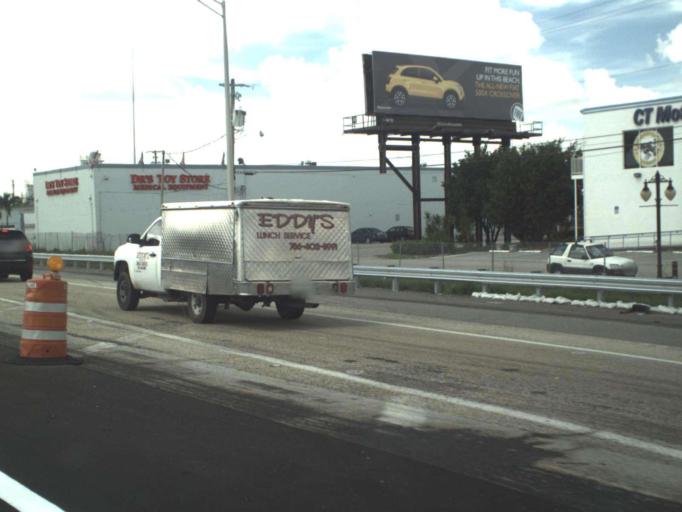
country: US
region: Florida
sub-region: Broward County
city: Pembroke Park
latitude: 25.9900
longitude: -80.1660
